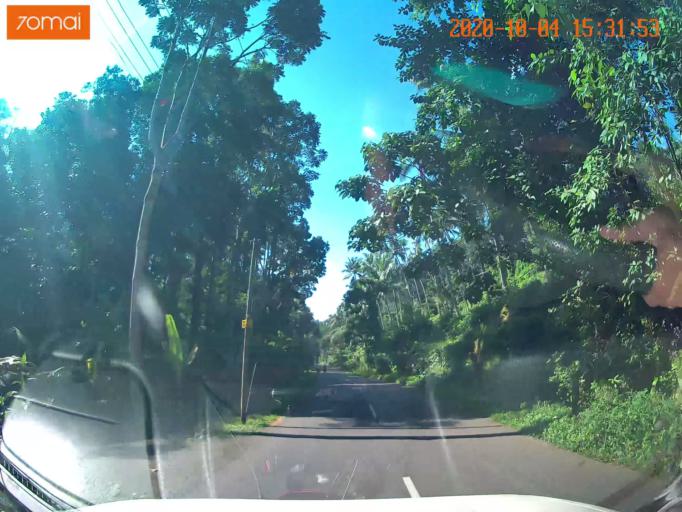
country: IN
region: Kerala
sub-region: Kottayam
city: Palackattumala
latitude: 9.7318
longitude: 76.6371
